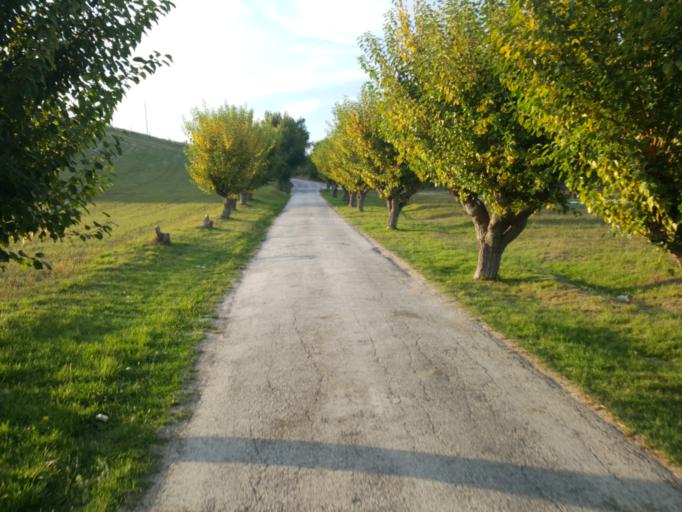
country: IT
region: The Marches
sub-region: Provincia di Ancona
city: Fabriano
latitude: 43.3478
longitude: 12.8422
